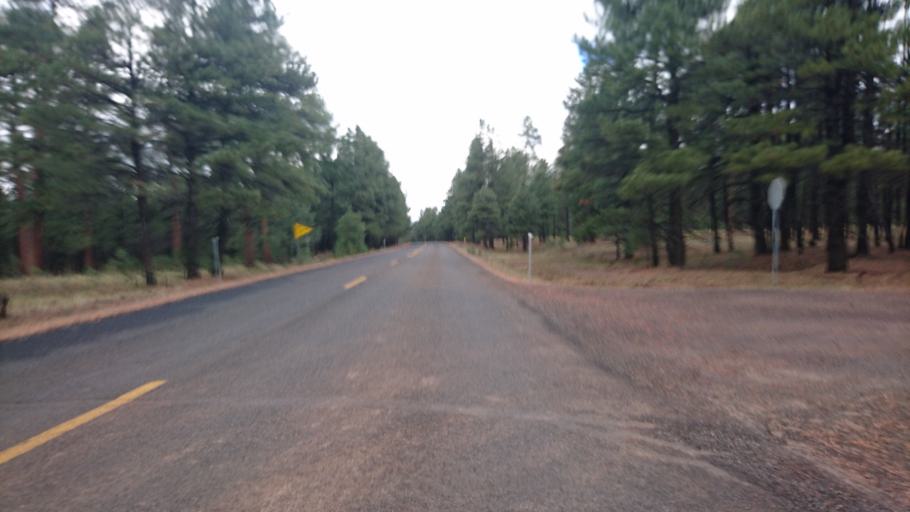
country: US
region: Arizona
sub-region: Coconino County
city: Parks
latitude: 35.2614
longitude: -111.8720
